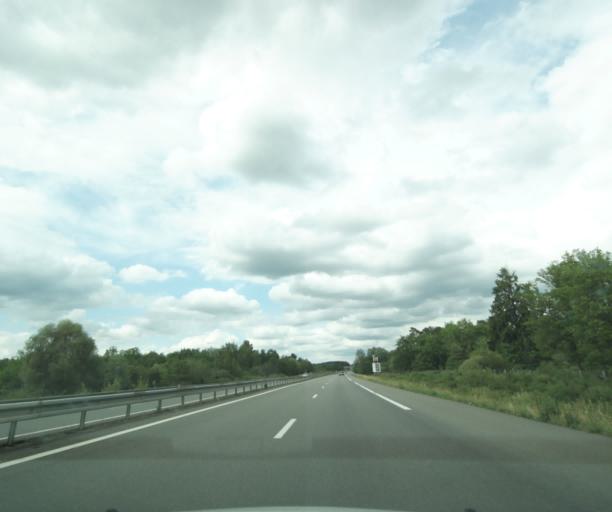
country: FR
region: Centre
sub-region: Departement du Loir-et-Cher
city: Theillay
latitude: 47.3381
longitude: 2.0477
